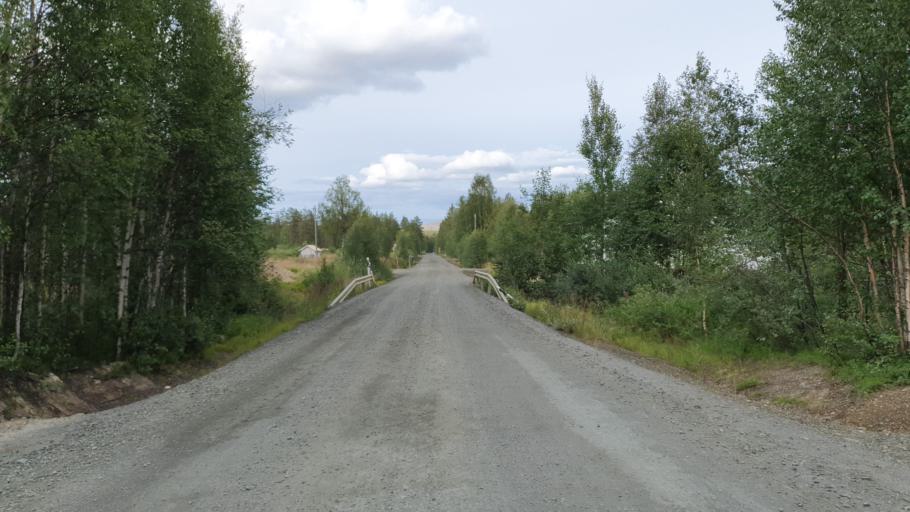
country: FI
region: Lapland
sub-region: Tunturi-Lappi
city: Kolari
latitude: 67.6225
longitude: 24.1614
